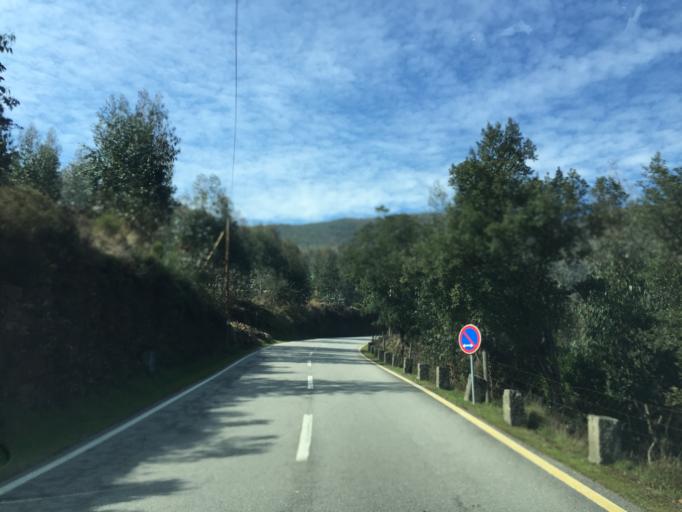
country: PT
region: Aveiro
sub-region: Arouca
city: Arouca
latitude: 40.9569
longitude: -8.1776
